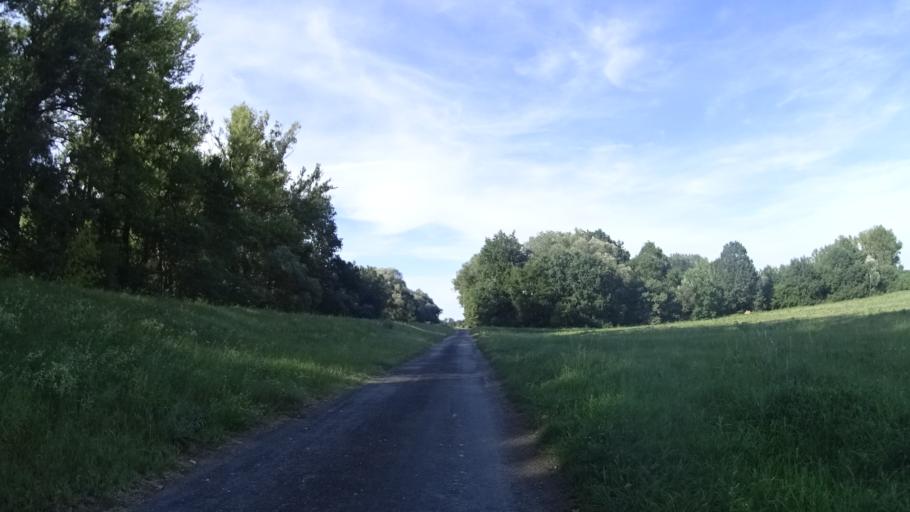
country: AT
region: Lower Austria
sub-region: Politischer Bezirk Ganserndorf
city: Drosing
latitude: 48.5432
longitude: 16.9604
